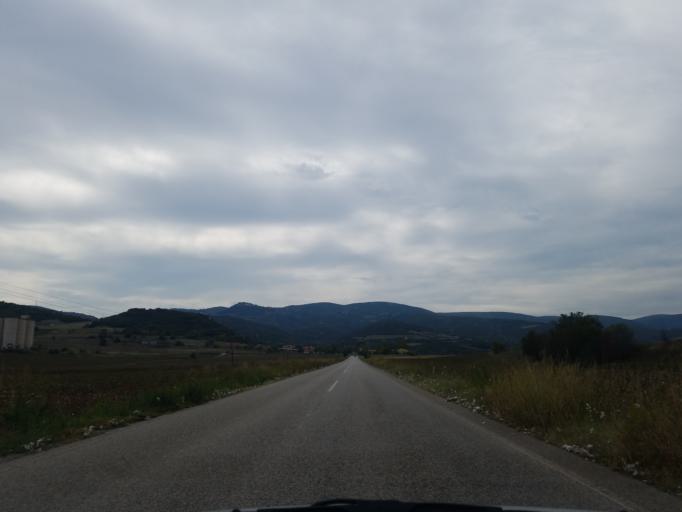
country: GR
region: Central Greece
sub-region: Nomos Fthiotidos
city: Domokos
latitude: 39.1635
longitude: 22.2942
